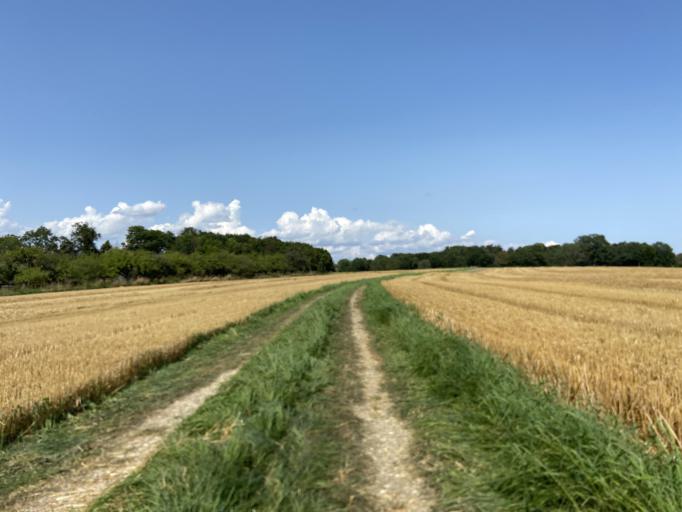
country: DE
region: Baden-Wuerttemberg
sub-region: Tuebingen Region
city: Sigmaringendorf
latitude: 48.0720
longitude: 9.2724
